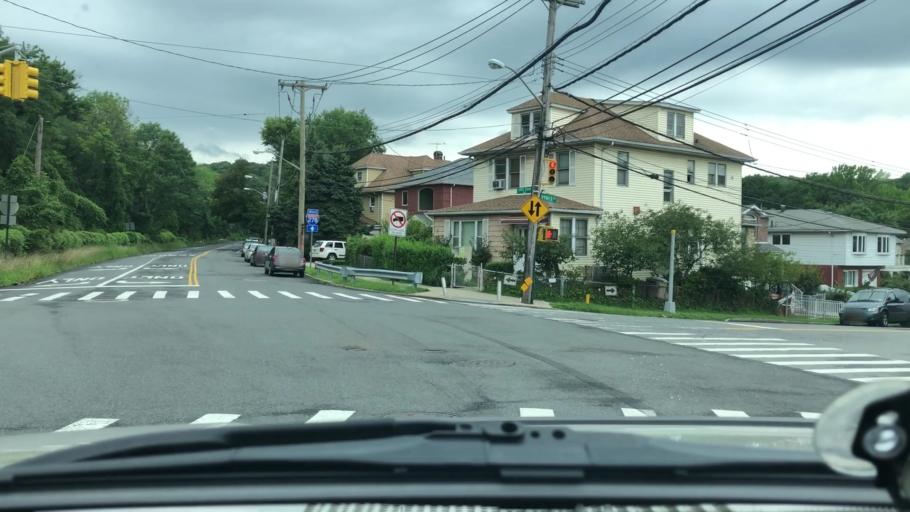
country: US
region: New Jersey
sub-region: Hudson County
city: Bayonne
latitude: 40.6112
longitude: -74.1054
